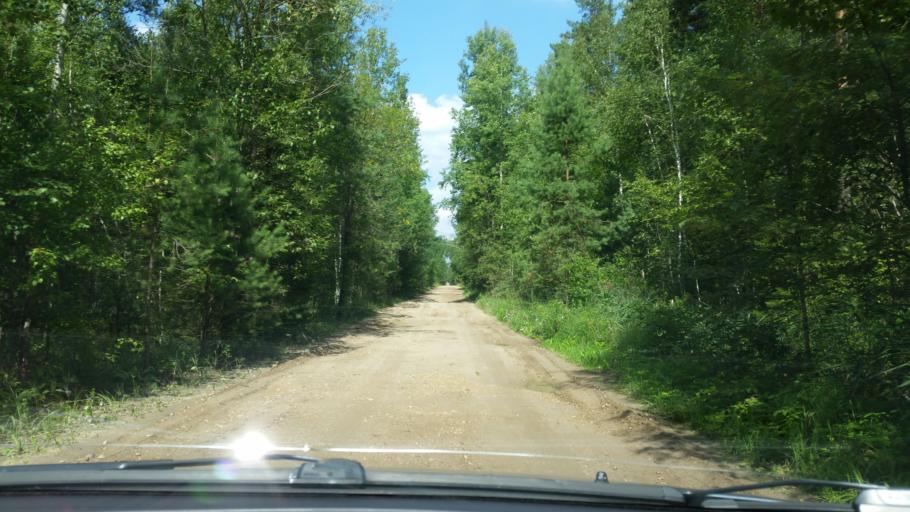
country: RU
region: Moskovskaya
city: Pushchino
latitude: 54.9074
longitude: 37.6856
